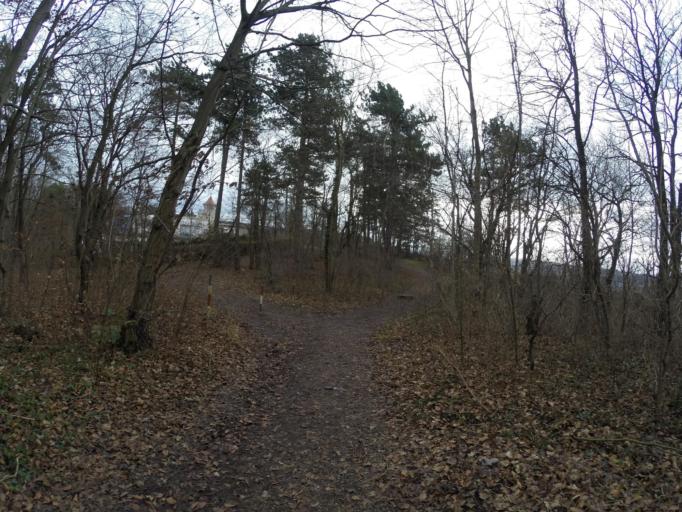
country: DE
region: Thuringia
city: Jena
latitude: 50.9369
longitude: 11.5786
